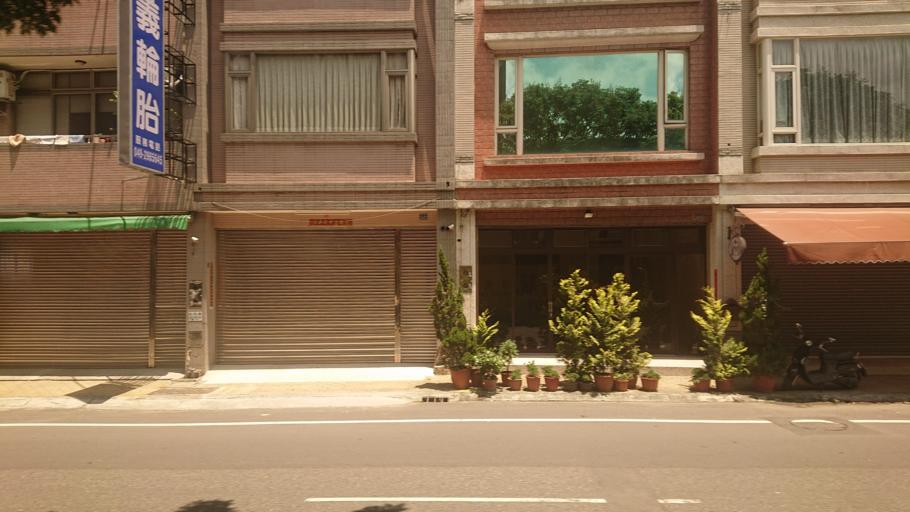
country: TW
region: Taiwan
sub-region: Nantou
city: Puli
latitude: 23.9733
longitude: 120.9691
